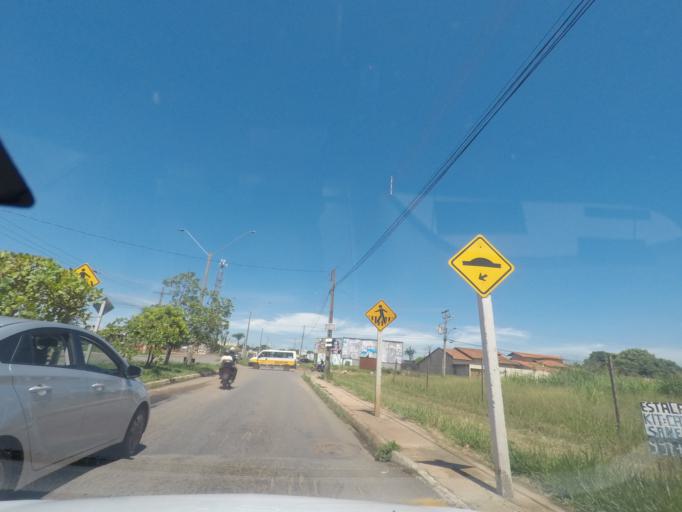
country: BR
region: Goias
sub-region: Aparecida De Goiania
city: Aparecida de Goiania
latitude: -16.7701
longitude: -49.3264
